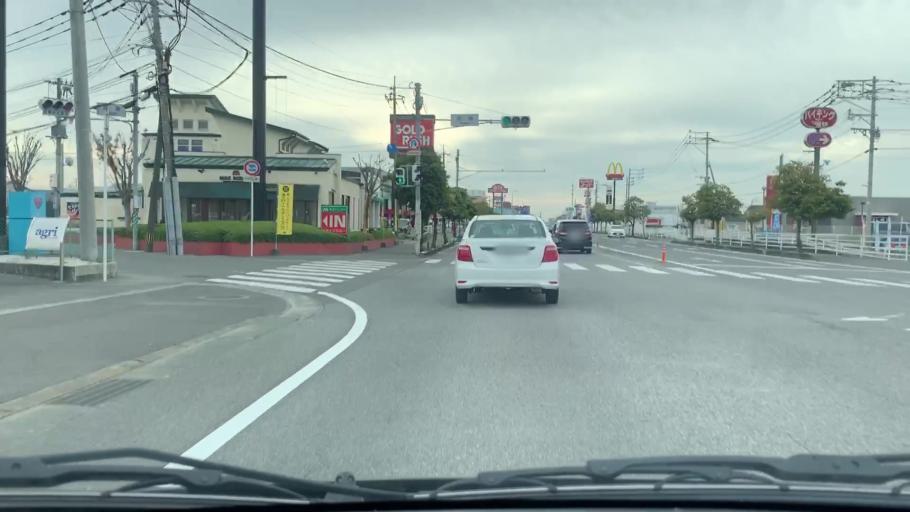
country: JP
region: Saga Prefecture
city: Saga-shi
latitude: 33.2944
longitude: 130.2840
